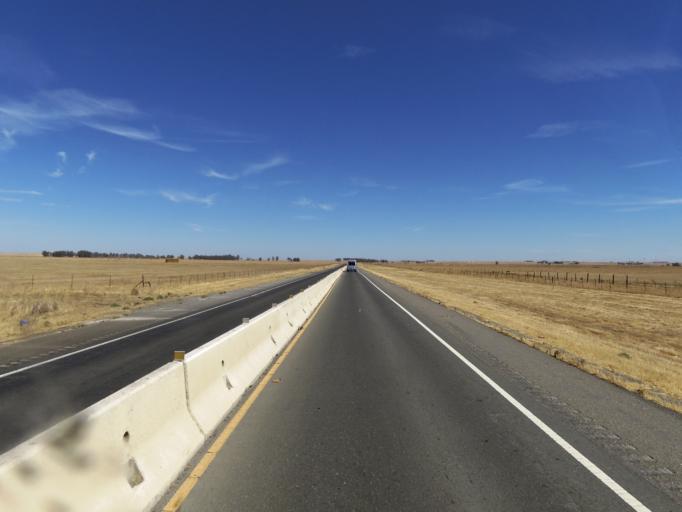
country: US
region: California
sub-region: Solano County
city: Suisun
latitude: 38.2284
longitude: -121.9384
